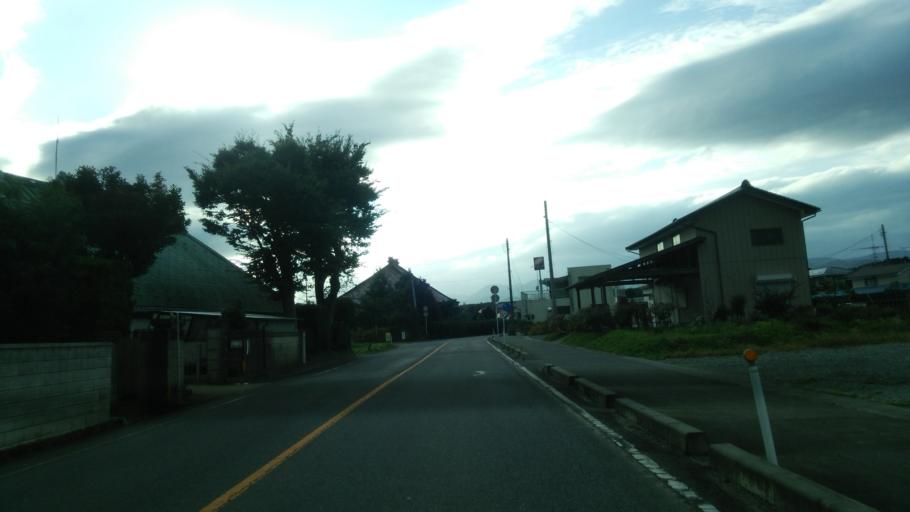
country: JP
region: Fukushima
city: Sukagawa
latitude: 37.3308
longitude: 140.2962
